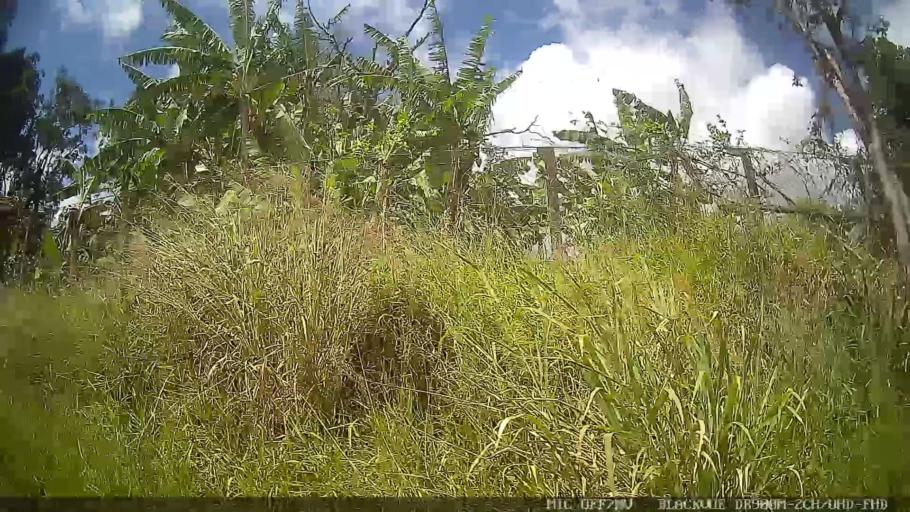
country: BR
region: Sao Paulo
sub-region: Braganca Paulista
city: Braganca Paulista
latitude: -22.8645
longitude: -46.6720
